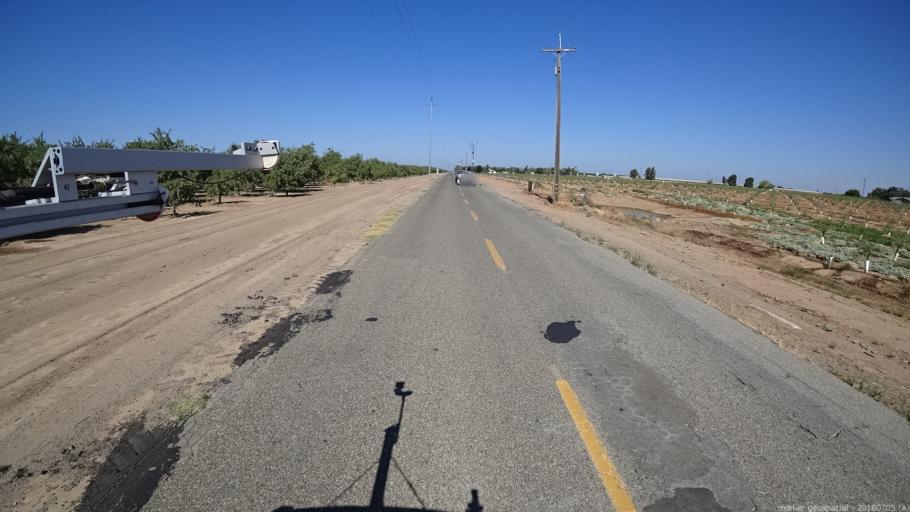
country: US
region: California
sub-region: Madera County
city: Fairmead
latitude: 37.1267
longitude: -120.1262
